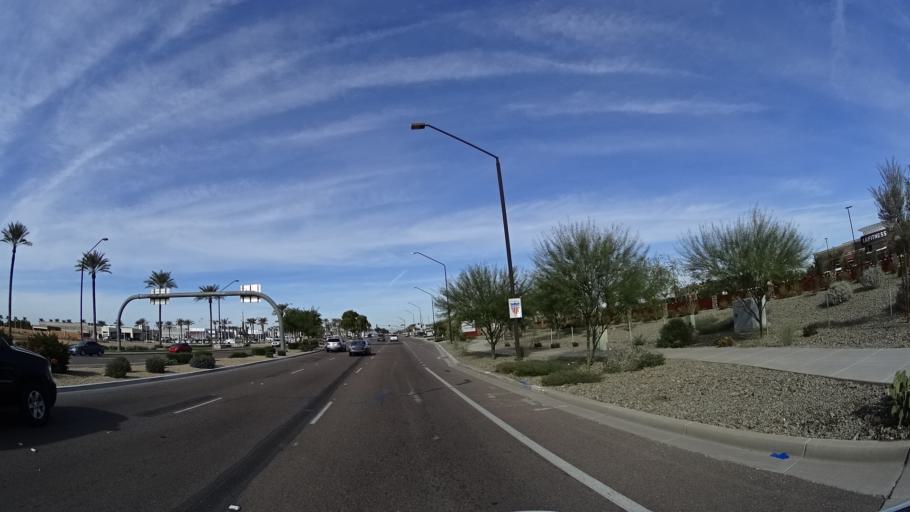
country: US
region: Arizona
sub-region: Maricopa County
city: Chandler
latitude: 33.2839
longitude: -111.7895
